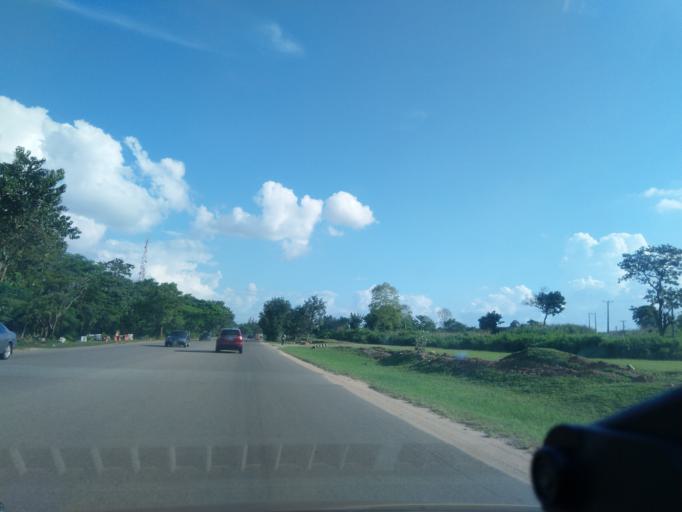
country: NG
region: Abuja Federal Capital Territory
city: Abuja
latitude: 9.0410
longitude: 7.4120
